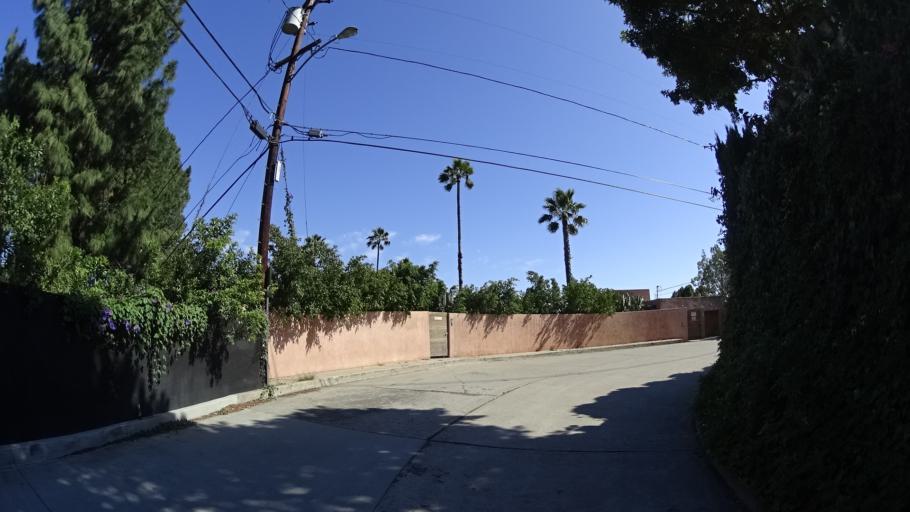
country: US
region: California
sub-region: Los Angeles County
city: Beverly Hills
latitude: 34.0929
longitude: -118.3891
